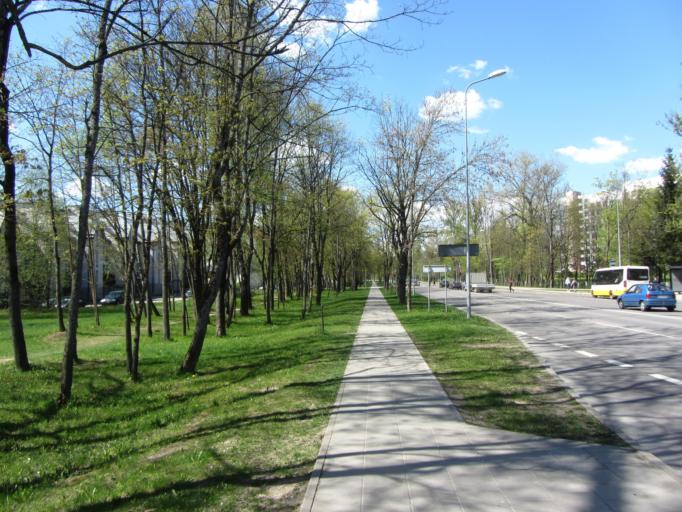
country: LT
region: Vilnius County
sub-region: Vilnius
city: Fabijoniskes
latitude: 54.7499
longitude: 25.2779
